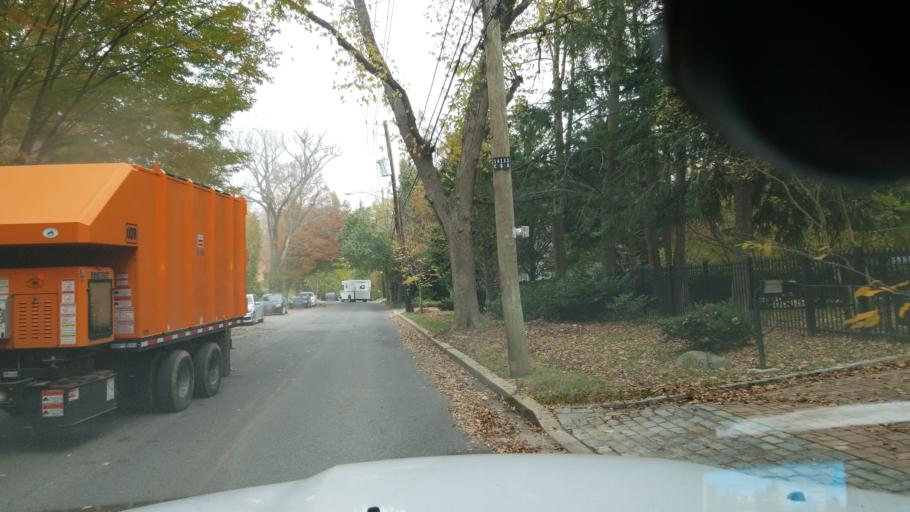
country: US
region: Maryland
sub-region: Montgomery County
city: Chevy Chase Village
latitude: 38.9479
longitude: -77.0629
